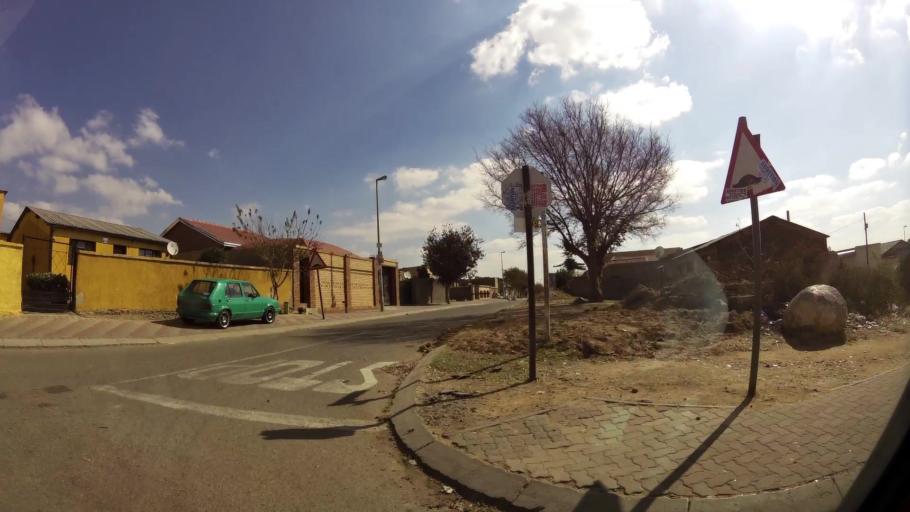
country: ZA
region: Gauteng
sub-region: Ekurhuleni Metropolitan Municipality
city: Tembisa
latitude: -26.0144
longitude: 28.1984
